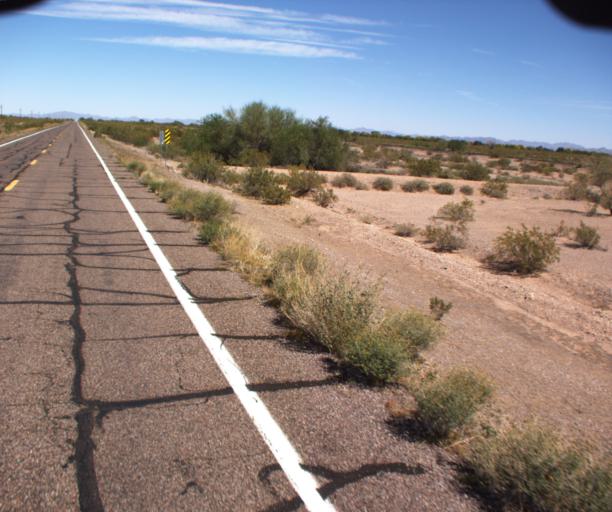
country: US
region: Arizona
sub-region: Maricopa County
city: Gila Bend
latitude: 32.8223
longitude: -112.7871
